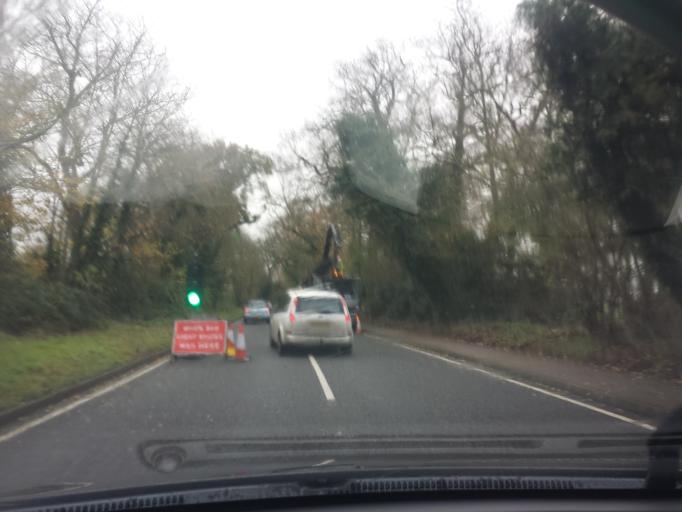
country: GB
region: England
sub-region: Essex
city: Little Clacton
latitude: 51.8534
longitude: 1.1632
